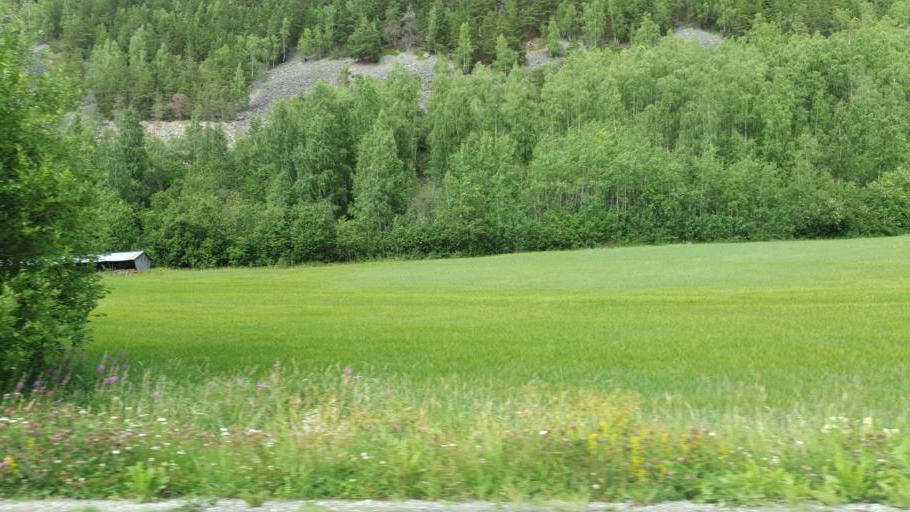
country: NO
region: Oppland
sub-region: Sel
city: Otta
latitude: 61.8423
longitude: 9.3916
